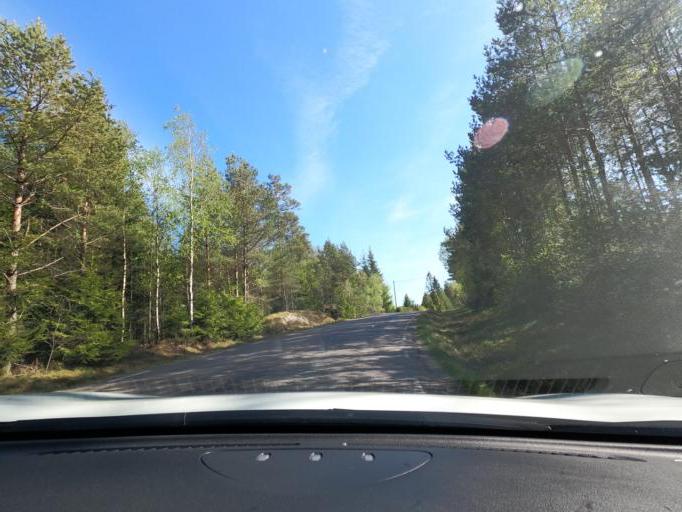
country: SE
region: Vaestra Goetaland
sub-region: Harryda Kommun
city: Hindas
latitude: 57.6675
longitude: 12.3538
